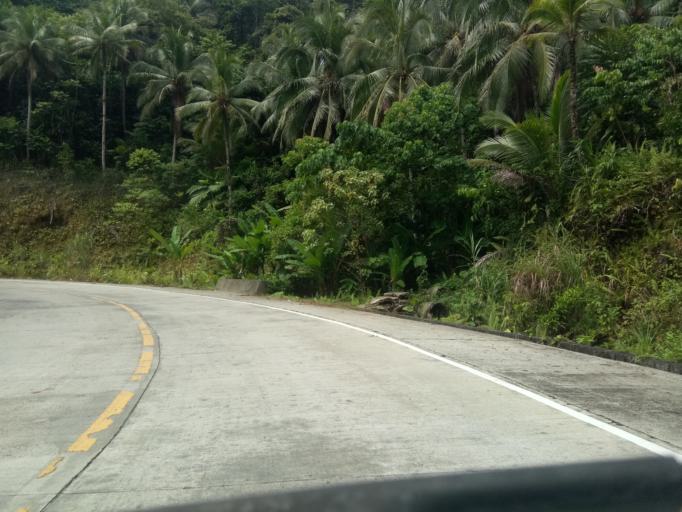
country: PH
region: Caraga
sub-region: Province of Surigao del Norte
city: Pilar
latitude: 9.8912
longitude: 126.0800
